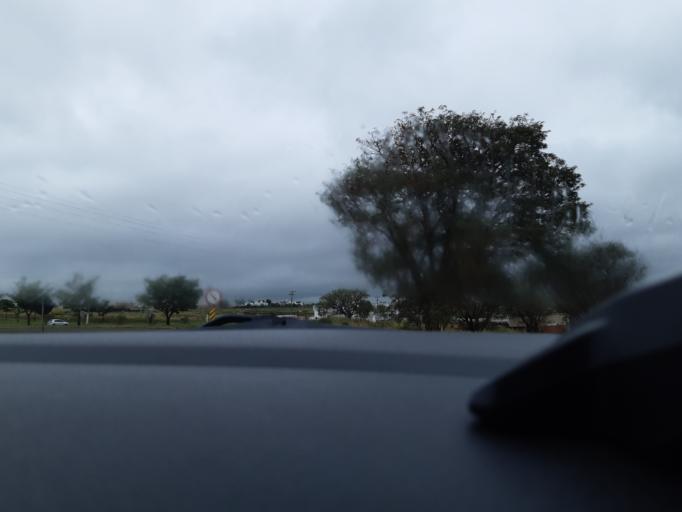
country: BR
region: Sao Paulo
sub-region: Ourinhos
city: Ourinhos
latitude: -22.9756
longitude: -49.9010
